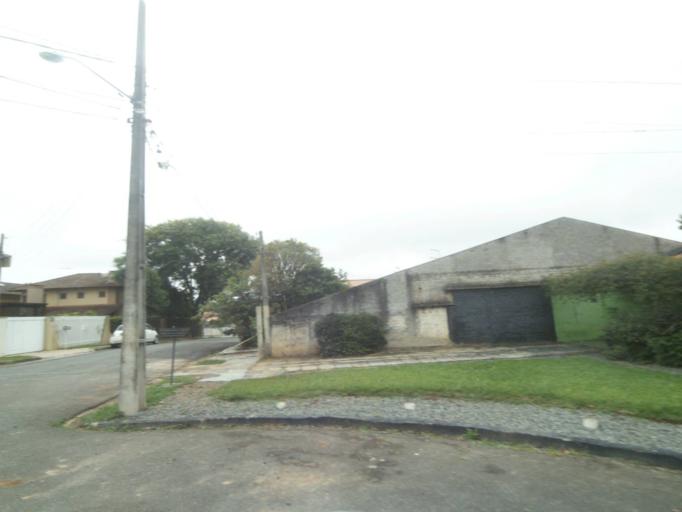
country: BR
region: Parana
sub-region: Curitiba
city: Curitiba
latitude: -25.4249
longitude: -49.3435
